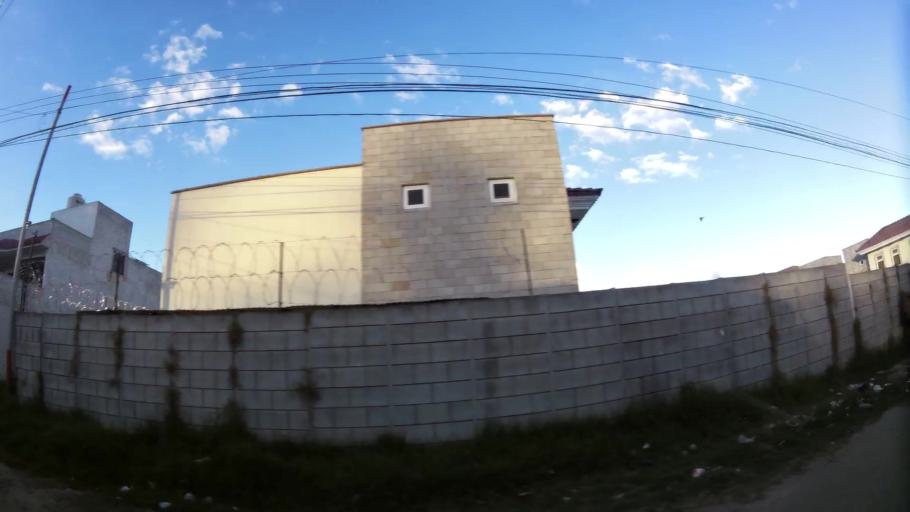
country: GT
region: Quetzaltenango
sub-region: Municipio de La Esperanza
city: La Esperanza
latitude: 14.8609
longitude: -91.5376
